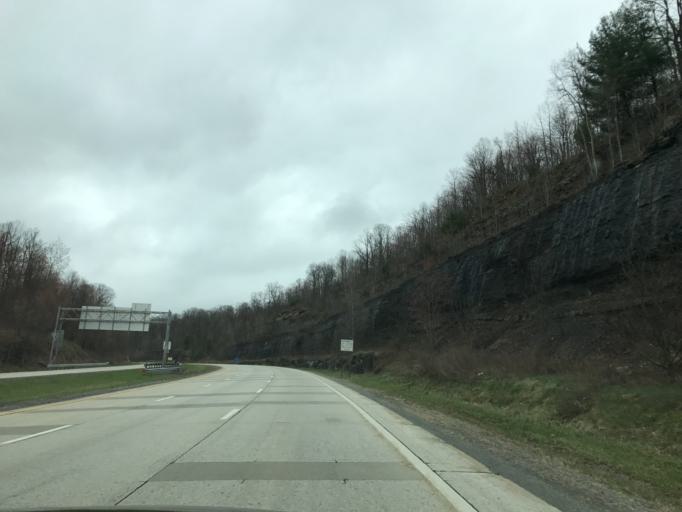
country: US
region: West Virginia
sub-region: Raleigh County
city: Beaver
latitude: 37.7372
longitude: -81.1786
